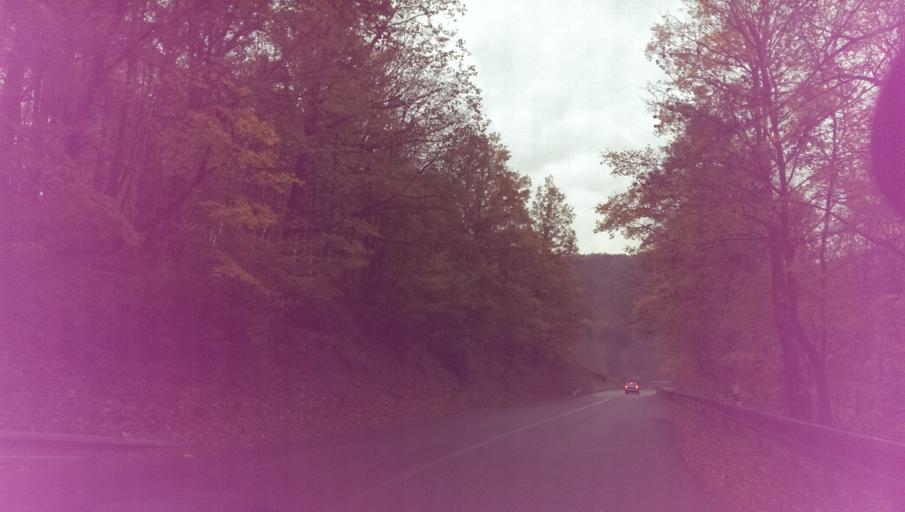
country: AT
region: Lower Austria
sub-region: Politischer Bezirk Hollabrunn
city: Hardegg
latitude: 48.8964
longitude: 15.8192
